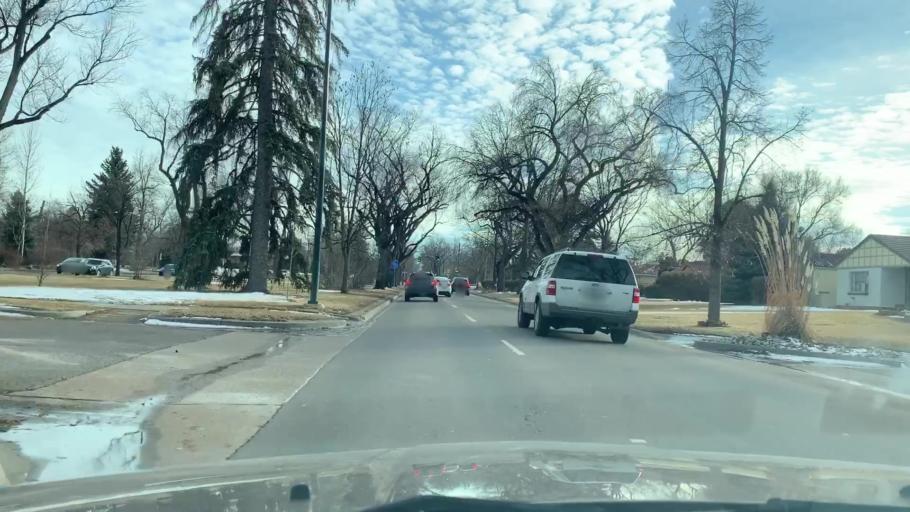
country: US
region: Colorado
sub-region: Arapahoe County
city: Glendale
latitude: 39.7269
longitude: -104.9128
